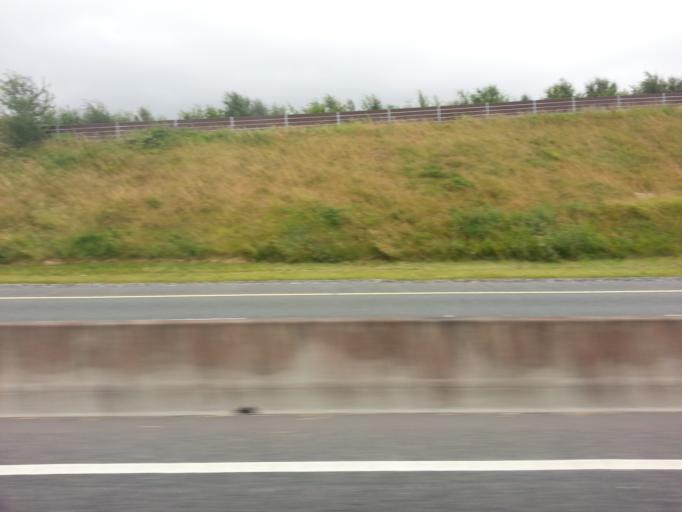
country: IE
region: Leinster
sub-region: Kildare
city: Castledermot
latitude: 52.8559
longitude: -6.8384
